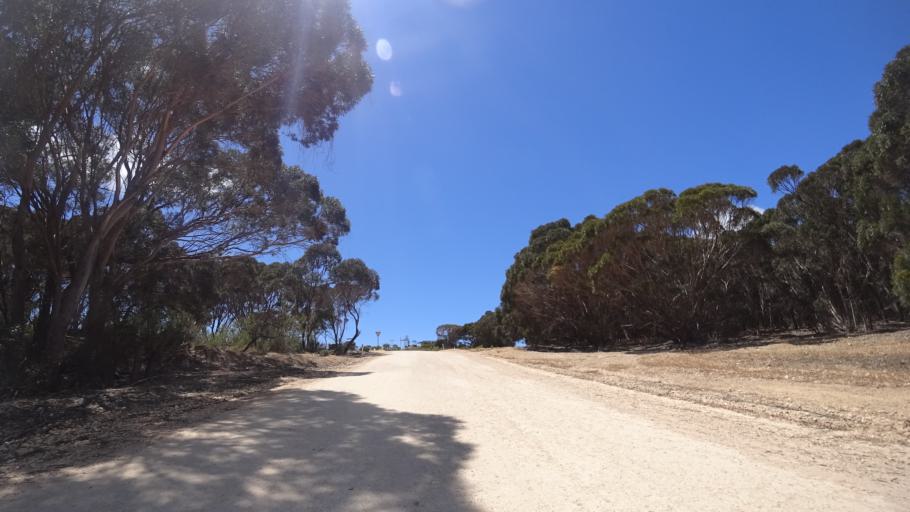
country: AU
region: South Australia
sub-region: Yankalilla
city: Normanville
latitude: -35.8112
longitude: 138.0717
